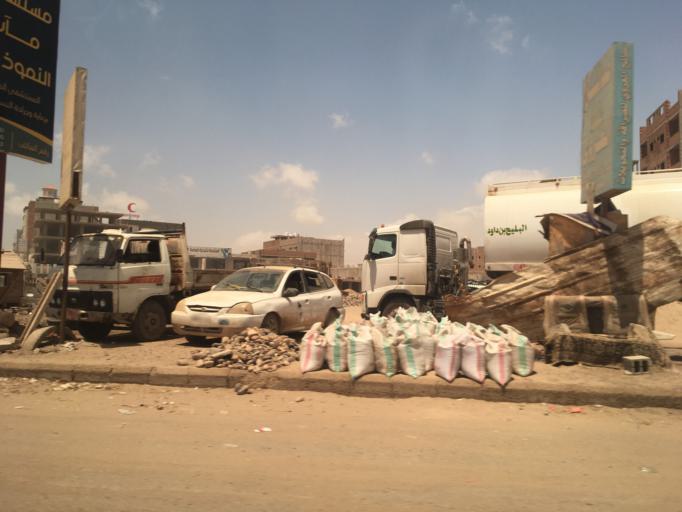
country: YE
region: Aden
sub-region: Al Mansura
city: Al Mansurah
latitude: 12.8686
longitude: 44.9706
